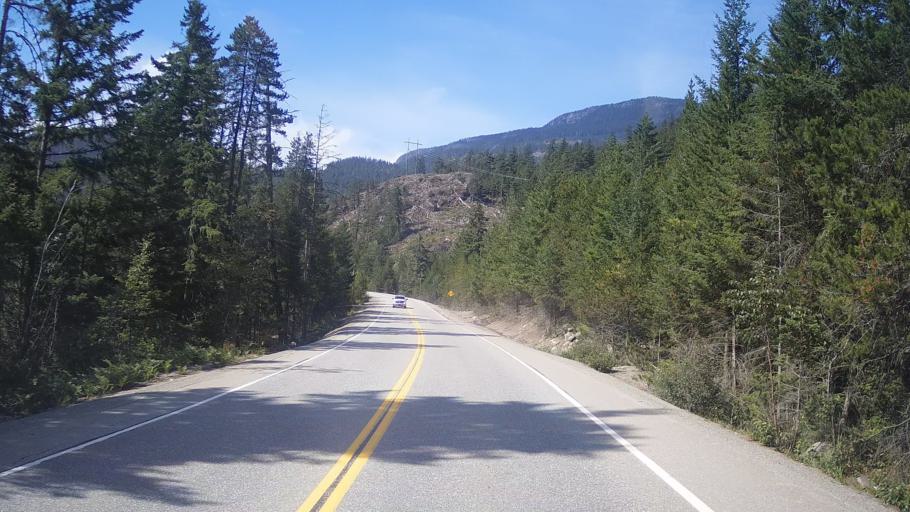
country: CA
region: British Columbia
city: Pemberton
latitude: 50.2761
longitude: -122.8650
